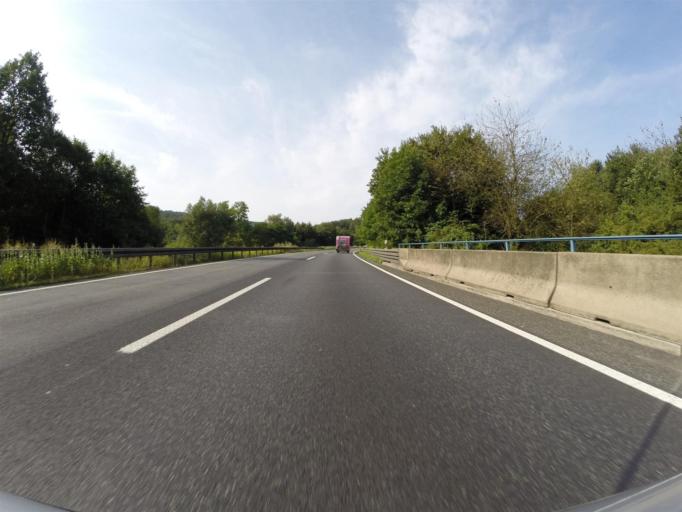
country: DE
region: Hesse
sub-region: Regierungsbezirk Kassel
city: Bad Hersfeld
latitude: 50.8592
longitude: 9.7705
